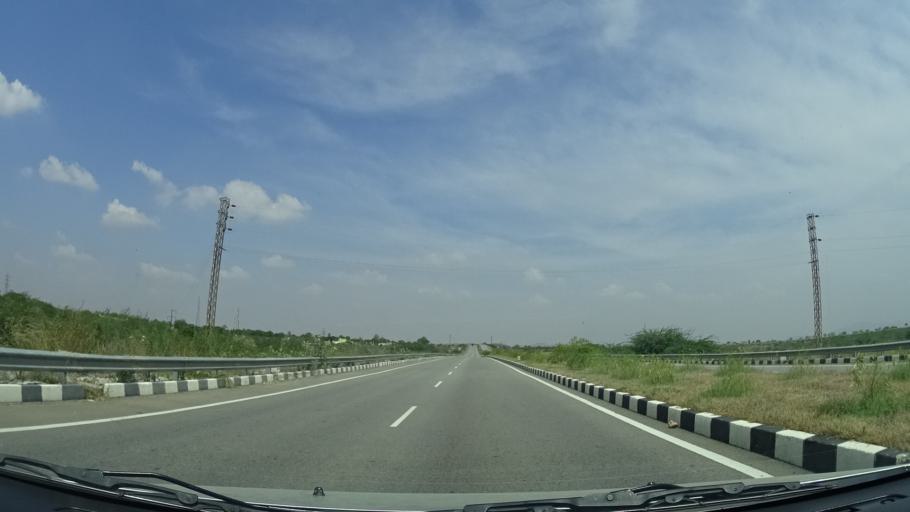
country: IN
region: Andhra Pradesh
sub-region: Anantapur
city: Dharmavaram
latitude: 14.3065
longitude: 77.6323
